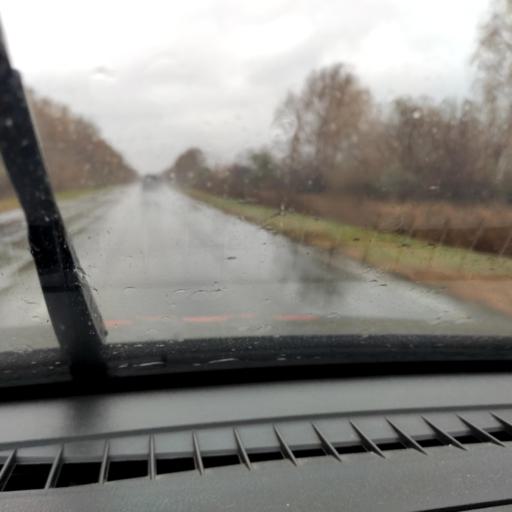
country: RU
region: Samara
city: Tol'yatti
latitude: 53.6675
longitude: 49.2771
